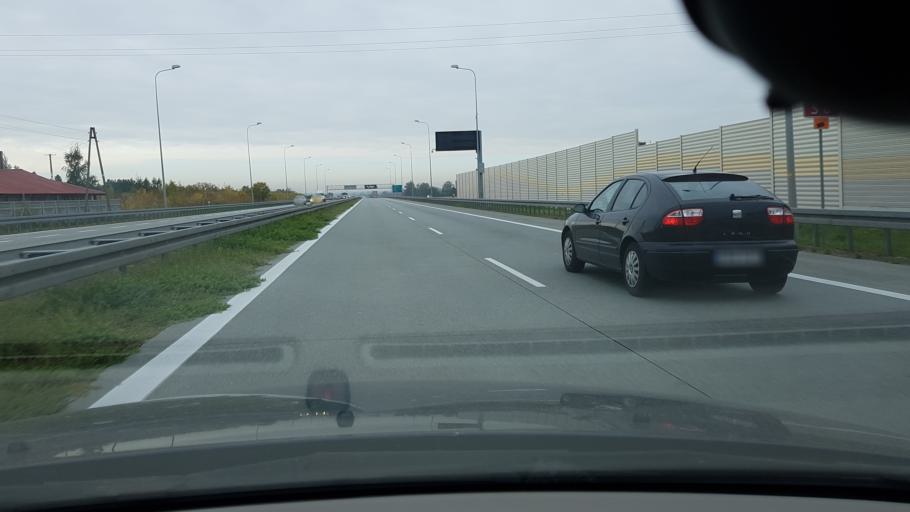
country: PL
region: Lodz Voivodeship
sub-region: Powiat rawski
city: Rawa Mazowiecka
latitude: 51.8022
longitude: 20.2990
